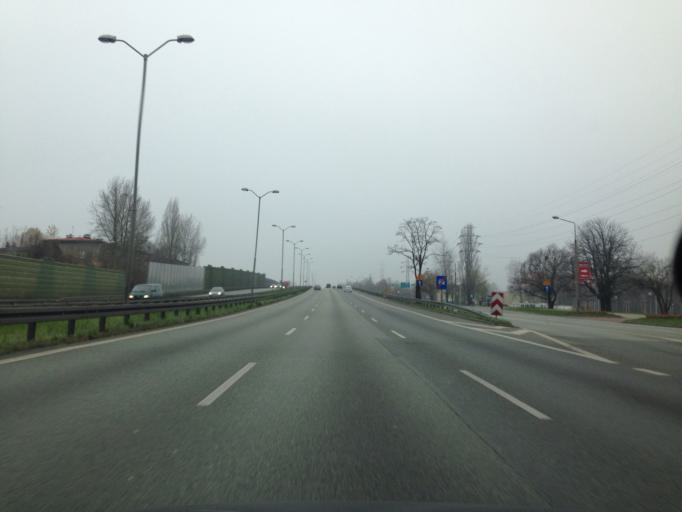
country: PL
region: Silesian Voivodeship
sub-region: Sosnowiec
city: Sosnowiec
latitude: 50.2762
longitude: 19.0750
